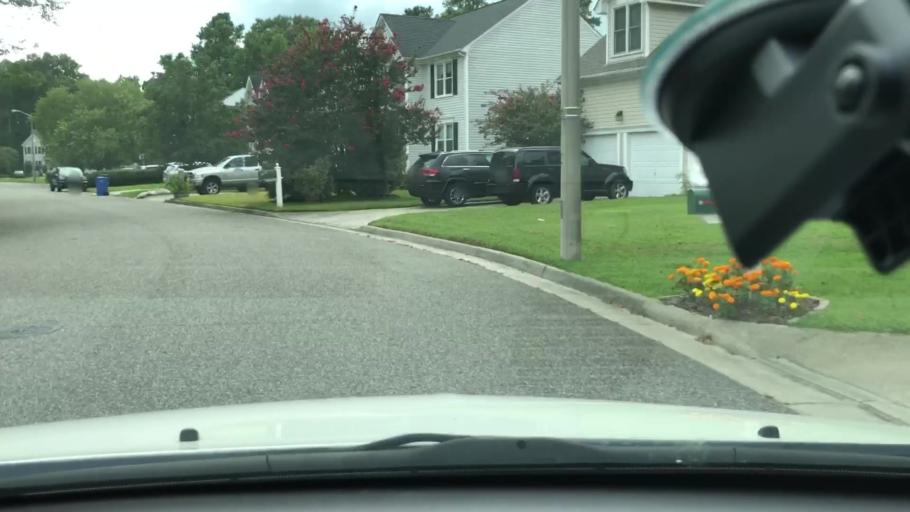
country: US
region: Virginia
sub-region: City of Chesapeake
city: Chesapeake
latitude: 36.7186
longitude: -76.2804
